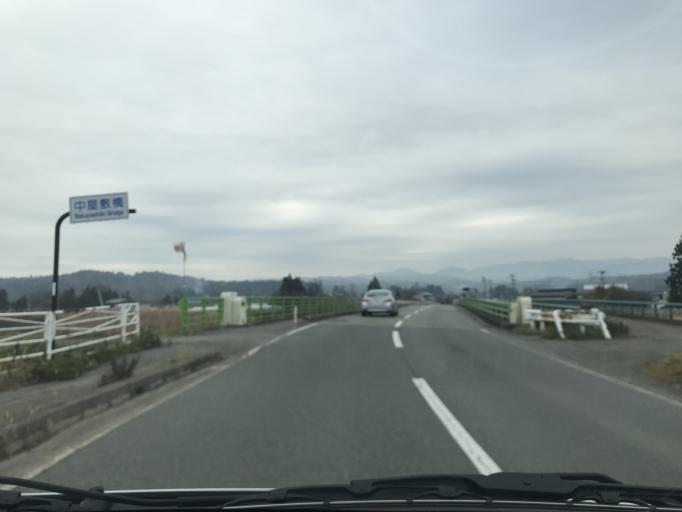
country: JP
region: Iwate
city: Mizusawa
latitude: 39.1603
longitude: 141.1848
